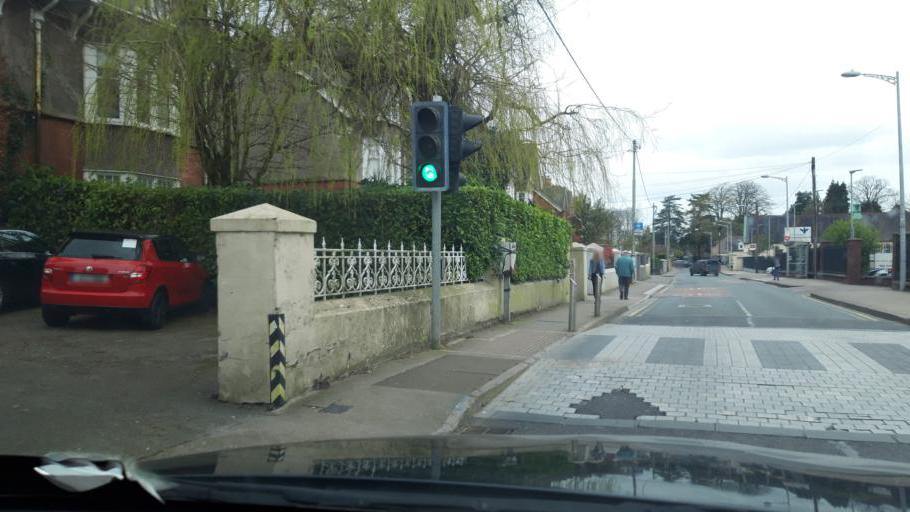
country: IE
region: Munster
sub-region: County Cork
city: Cork
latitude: 51.8913
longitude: -8.4967
